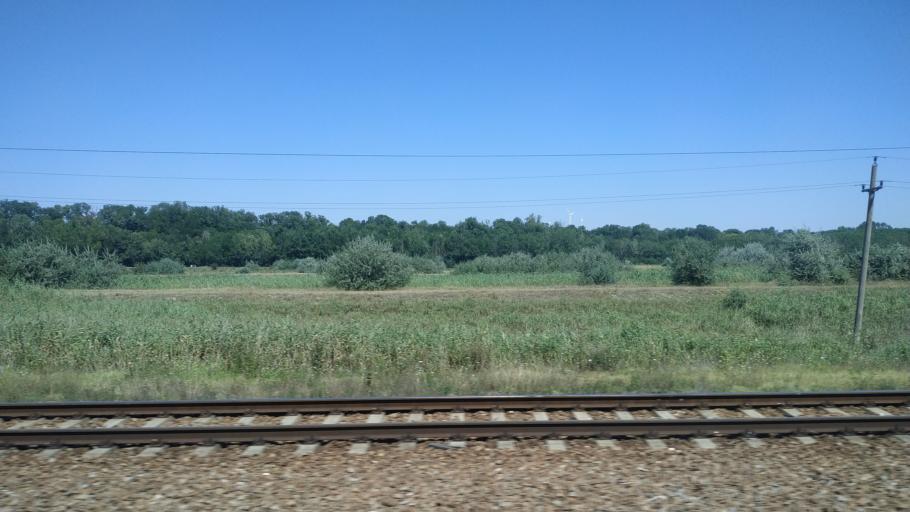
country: RO
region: Constanta
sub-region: Comuna Mircea Voda
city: Mircea Voda
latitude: 44.2653
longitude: 28.1506
